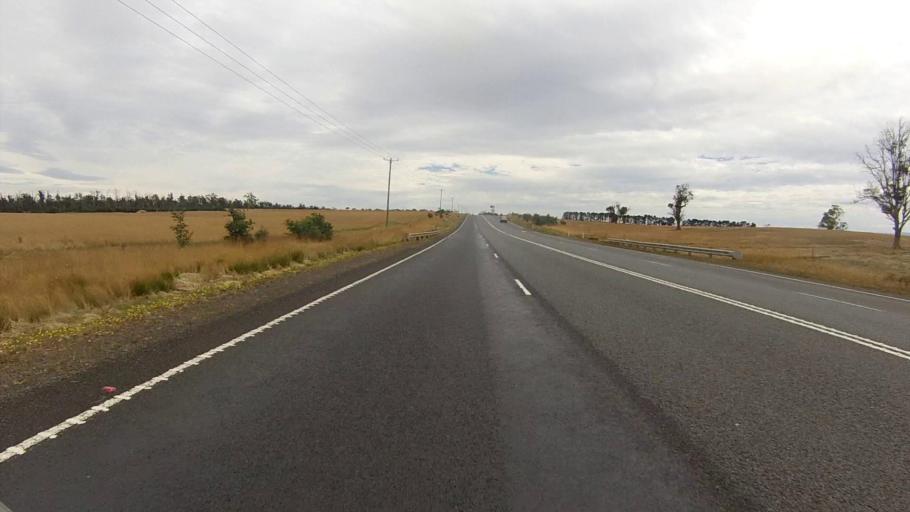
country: AU
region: Tasmania
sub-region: Northern Midlands
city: Evandale
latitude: -41.7177
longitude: 147.3088
